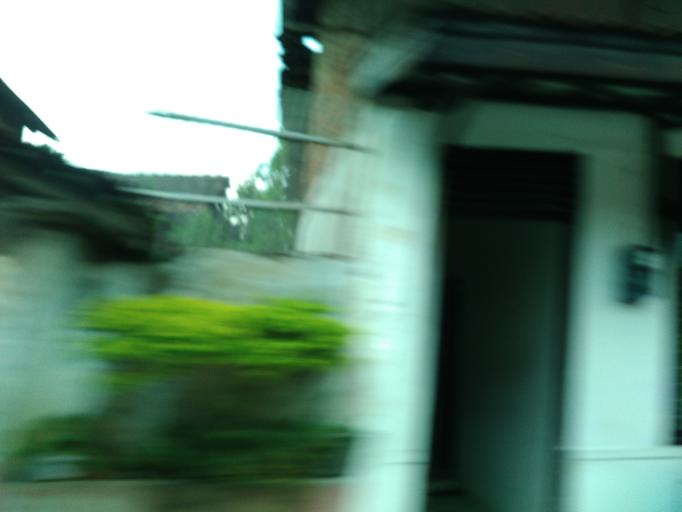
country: ID
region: Central Java
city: Delanggu
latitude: -7.6234
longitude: 110.7045
